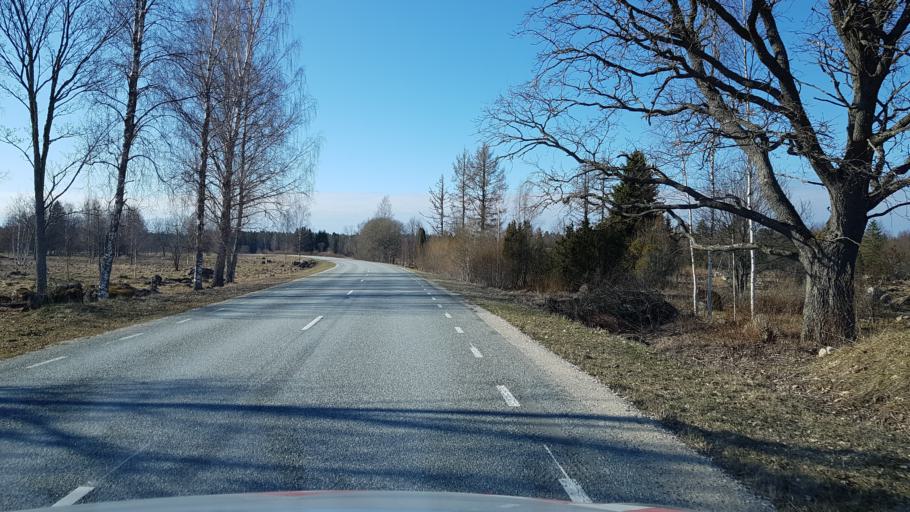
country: EE
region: Laeaene-Virumaa
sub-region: Kadrina vald
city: Kadrina
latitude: 59.5387
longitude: 26.0435
